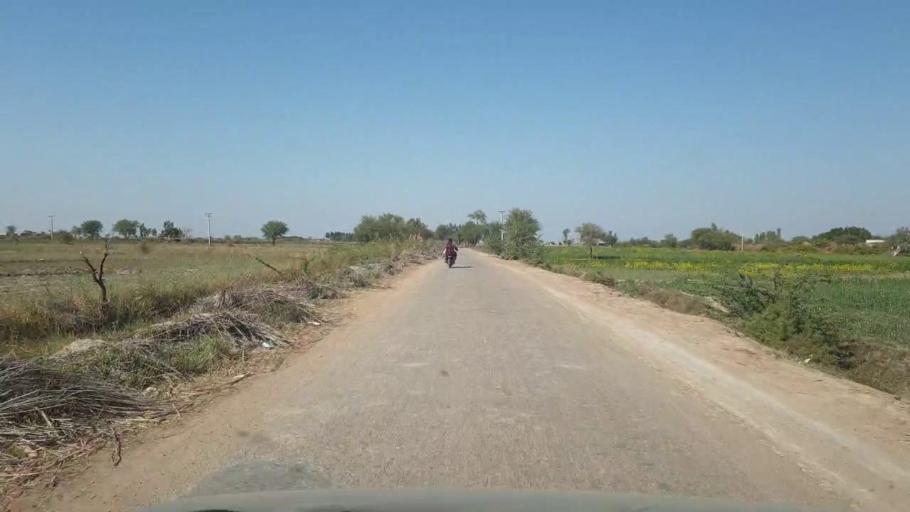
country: PK
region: Sindh
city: Samaro
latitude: 25.3620
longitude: 69.3190
